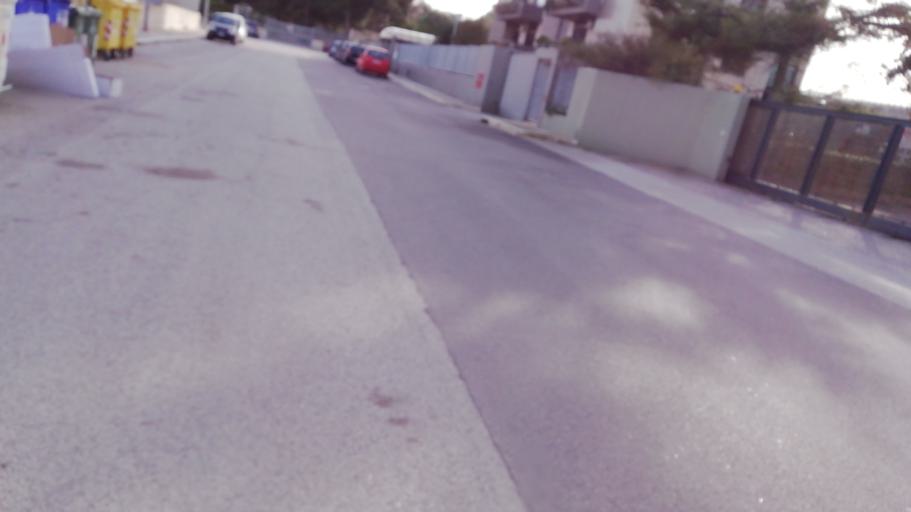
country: IT
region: Apulia
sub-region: Provincia di Bari
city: Triggiano
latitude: 41.1016
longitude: 16.9144
